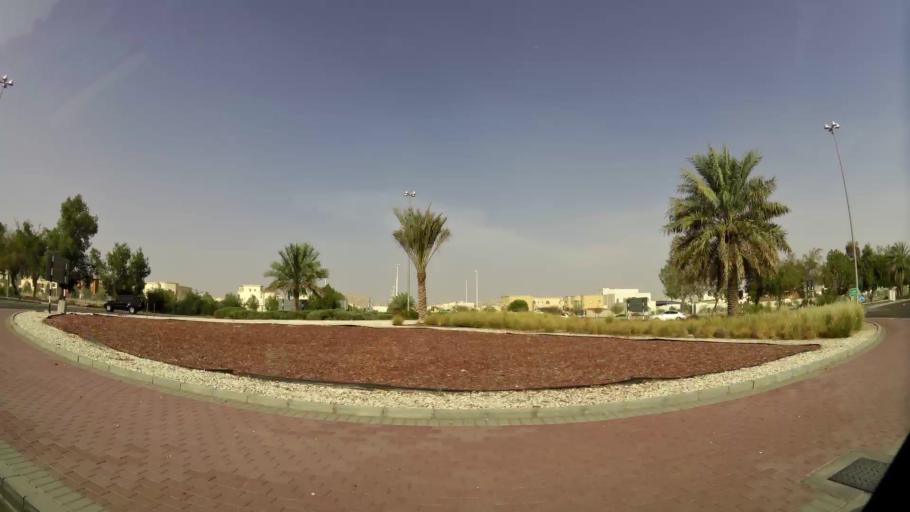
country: AE
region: Abu Dhabi
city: Al Ain
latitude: 24.1526
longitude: 55.7121
